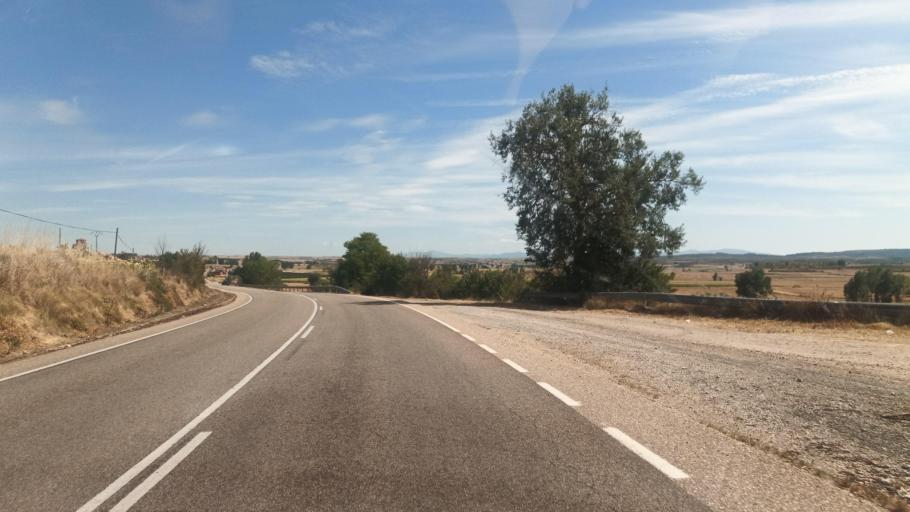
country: ES
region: Castille and Leon
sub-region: Provincia de Burgos
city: Quintanabureba
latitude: 42.6227
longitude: -3.3707
